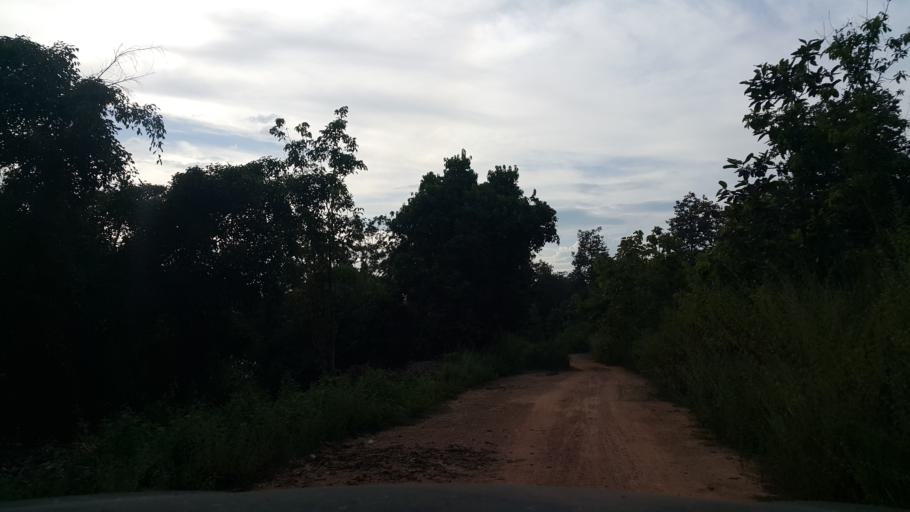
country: TH
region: Chiang Mai
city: San Sai
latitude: 18.9229
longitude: 99.0706
